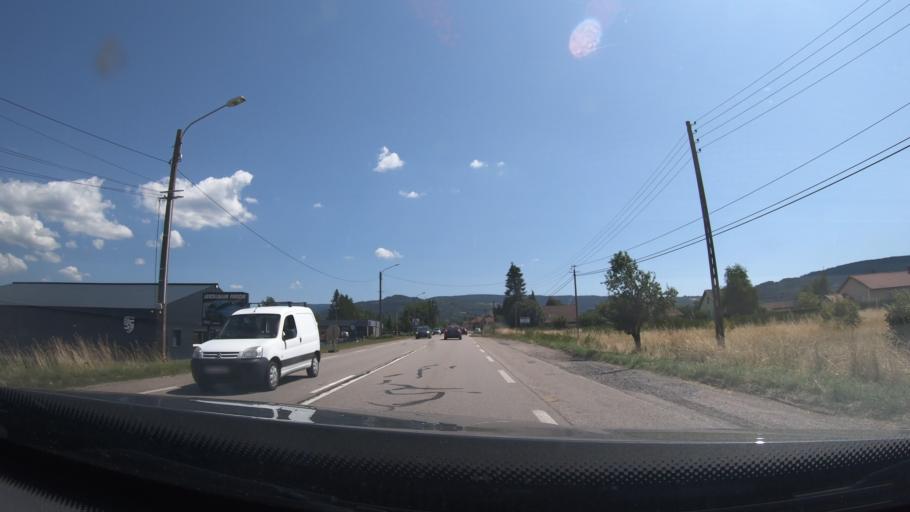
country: FR
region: Lorraine
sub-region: Departement des Vosges
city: Saint-Leonard
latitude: 48.2034
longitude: 6.9447
